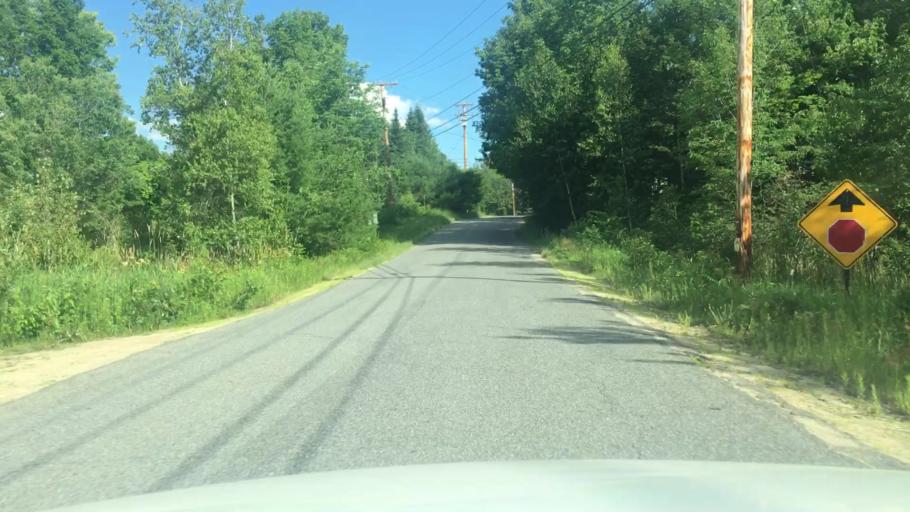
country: US
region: Maine
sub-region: Franklin County
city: Wilton
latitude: 44.5988
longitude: -70.2199
